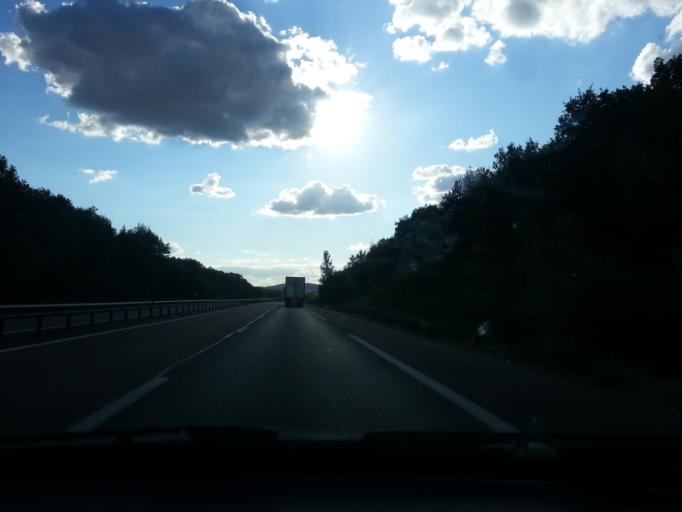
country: FR
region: Bourgogne
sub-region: Departement de Saone-et-Loire
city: Chatenoy-le-Royal
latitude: 46.7570
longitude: 4.7878
